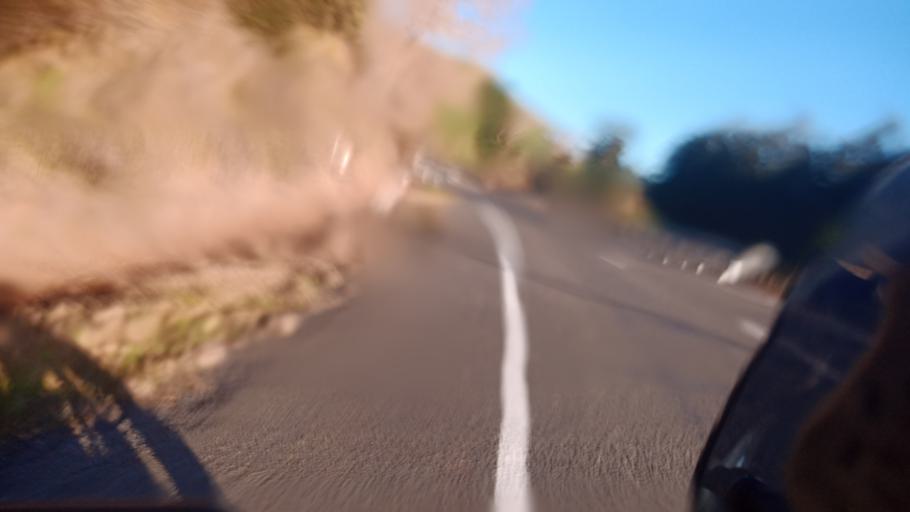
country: NZ
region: Hawke's Bay
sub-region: Wairoa District
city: Wairoa
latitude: -39.0159
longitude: 177.3550
